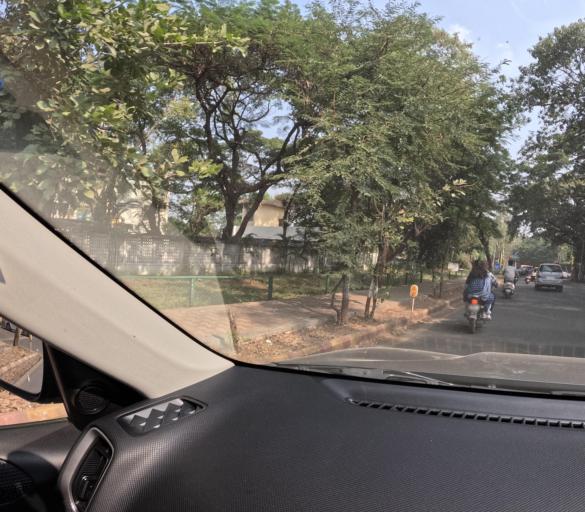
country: IN
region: Maharashtra
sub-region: Pune Division
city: Pune
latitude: 18.5235
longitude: 73.8849
